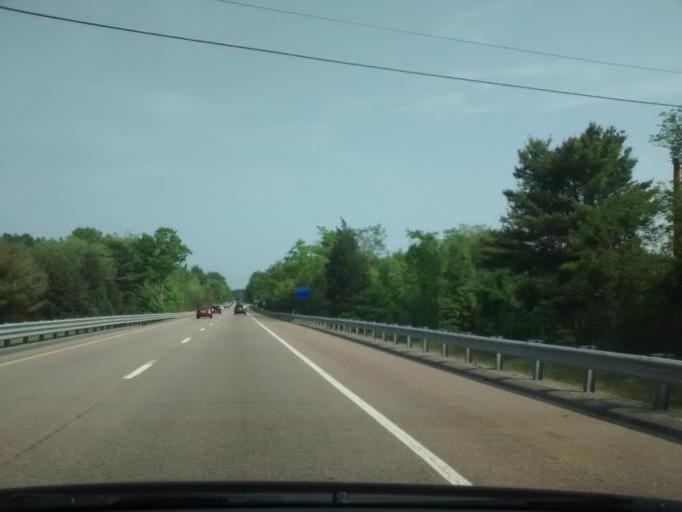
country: US
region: Massachusetts
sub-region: Plymouth County
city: West Wareham
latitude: 41.8019
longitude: -70.7634
